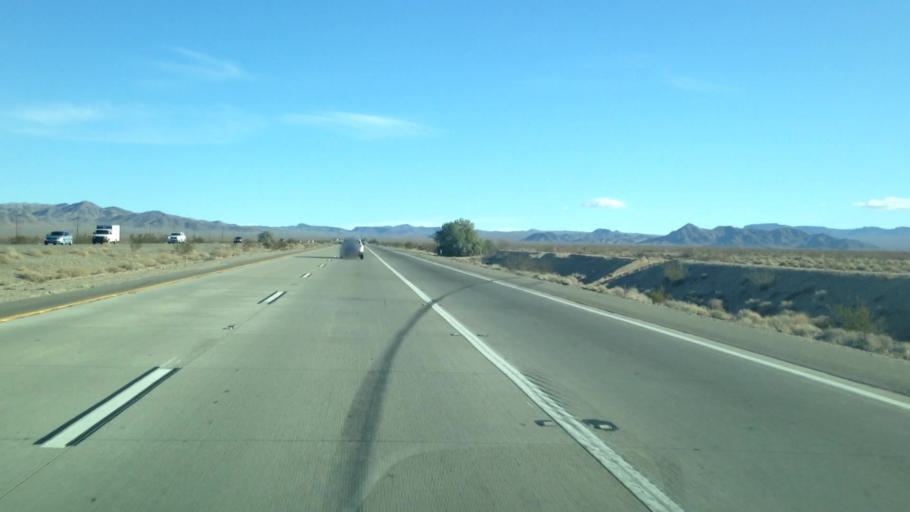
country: US
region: Nevada
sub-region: Clark County
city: Sandy Valley
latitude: 35.2977
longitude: -116.0237
